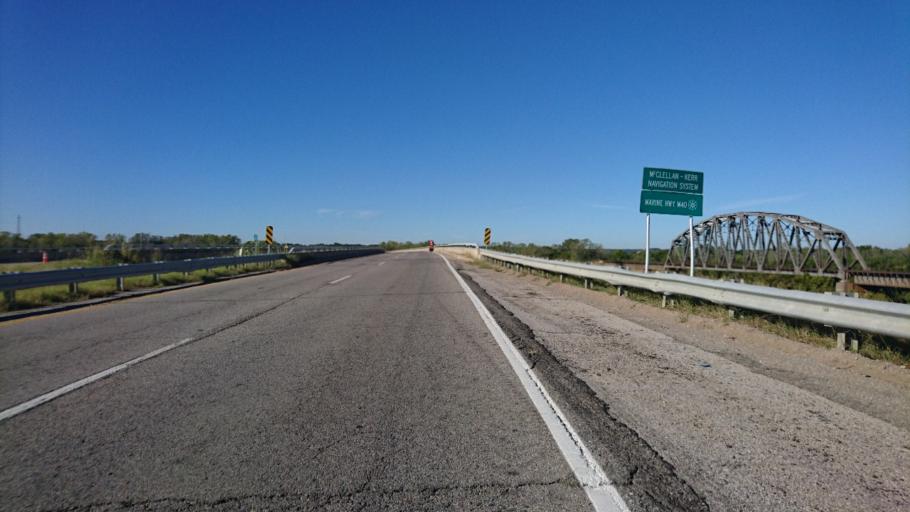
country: US
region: Oklahoma
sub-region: Rogers County
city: Verdigris
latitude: 36.2165
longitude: -95.7192
